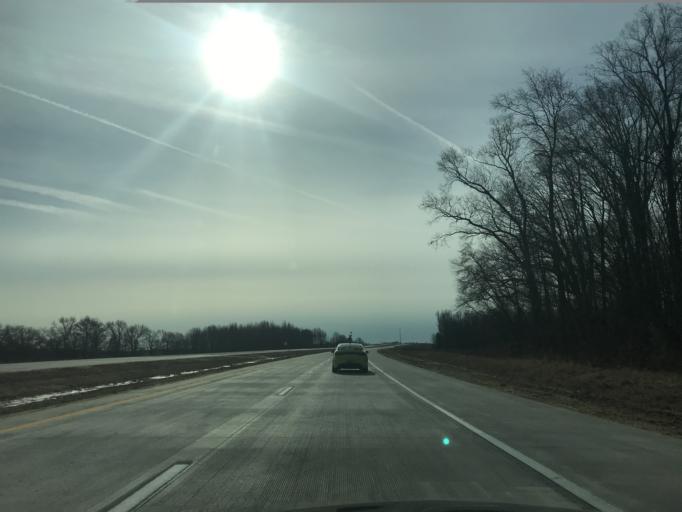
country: US
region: Delaware
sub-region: New Castle County
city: Middletown
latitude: 39.5141
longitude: -75.6916
